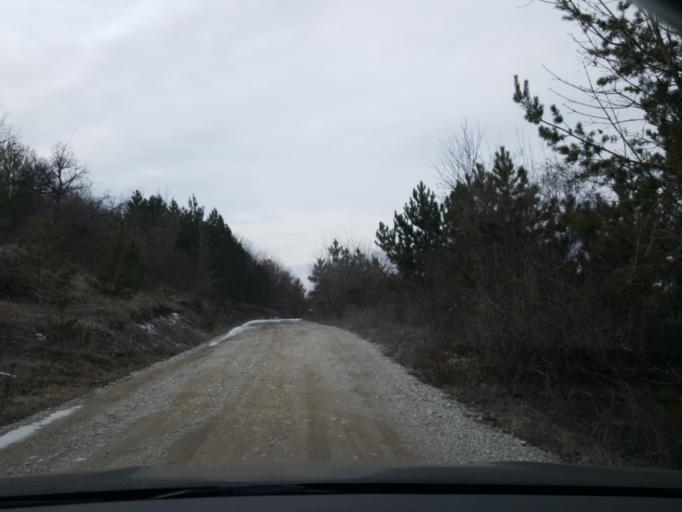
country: RS
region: Central Serbia
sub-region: Pirotski Okrug
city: Dimitrovgrad
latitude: 43.0001
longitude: 22.7496
